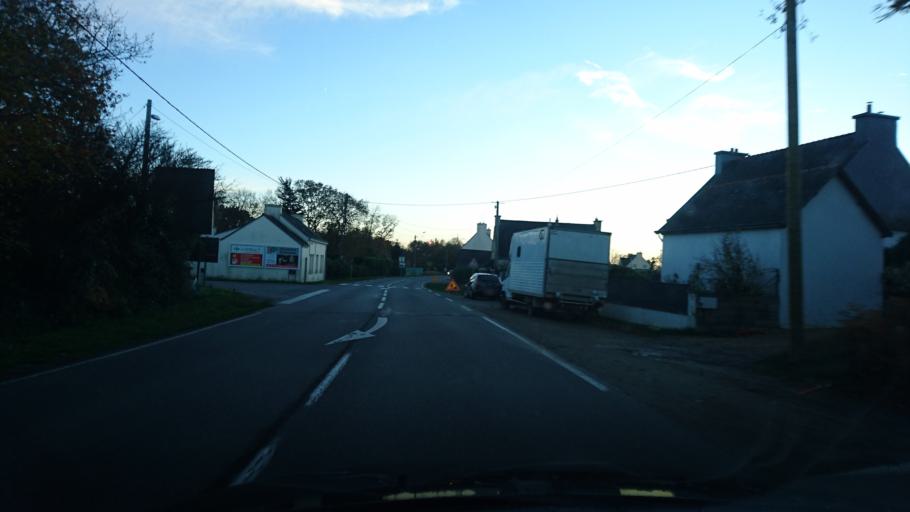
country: FR
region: Brittany
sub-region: Departement du Finistere
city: Quimperle
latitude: 47.8584
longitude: -3.5652
